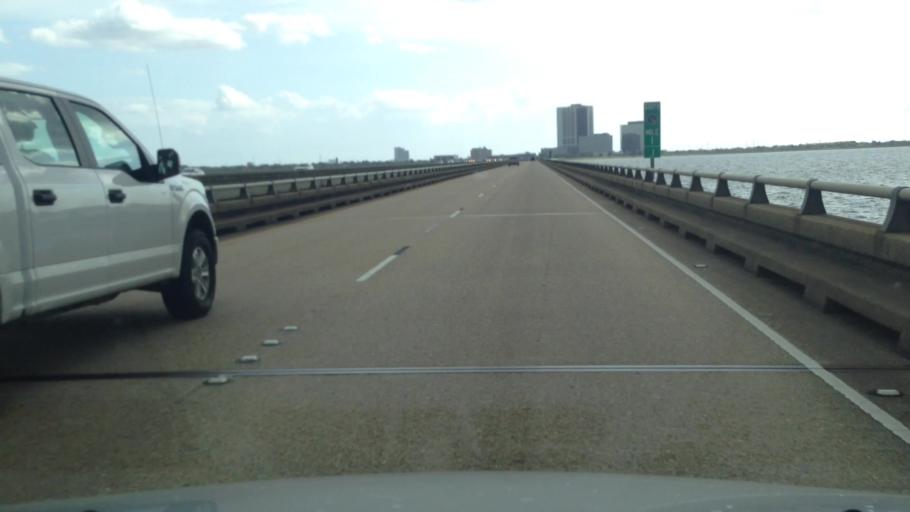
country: US
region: Louisiana
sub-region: Jefferson Parish
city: Metairie
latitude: 30.0377
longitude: -90.1513
